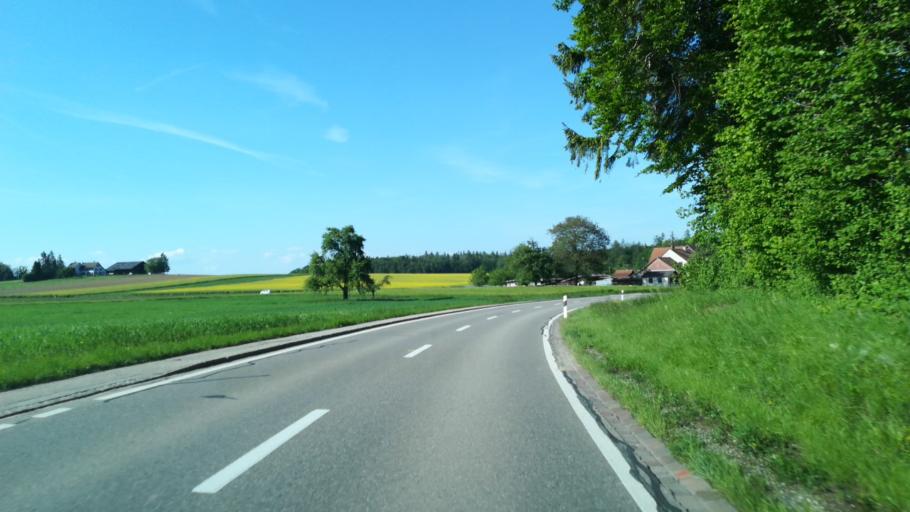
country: CH
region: Zurich
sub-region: Bezirk Andelfingen
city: Kleinandelfingen
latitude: 47.6211
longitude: 8.7382
